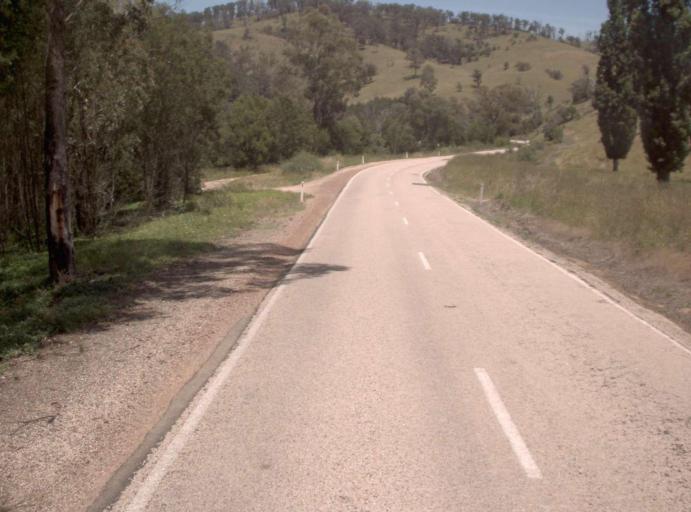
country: AU
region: Victoria
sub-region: East Gippsland
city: Lakes Entrance
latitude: -37.5219
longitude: 147.8481
